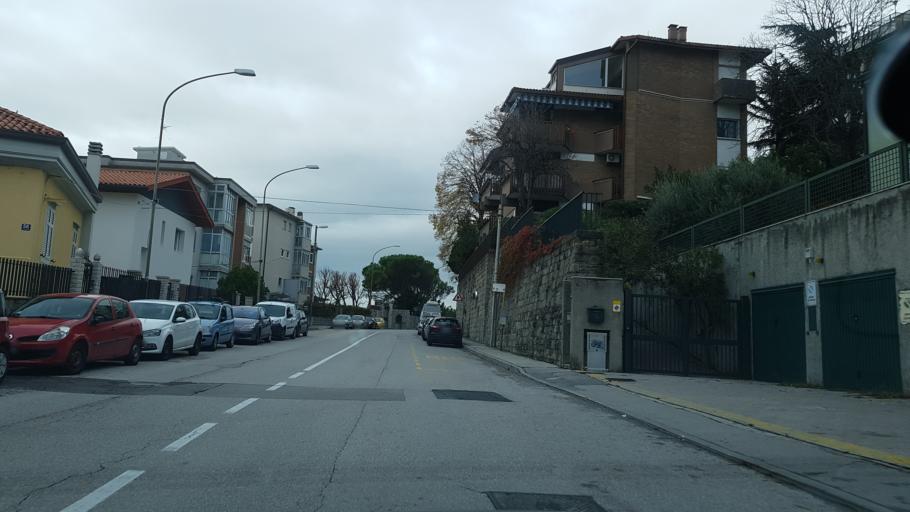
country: IT
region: Friuli Venezia Giulia
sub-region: Provincia di Trieste
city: Villa Opicina
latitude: 45.6710
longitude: 13.7607
